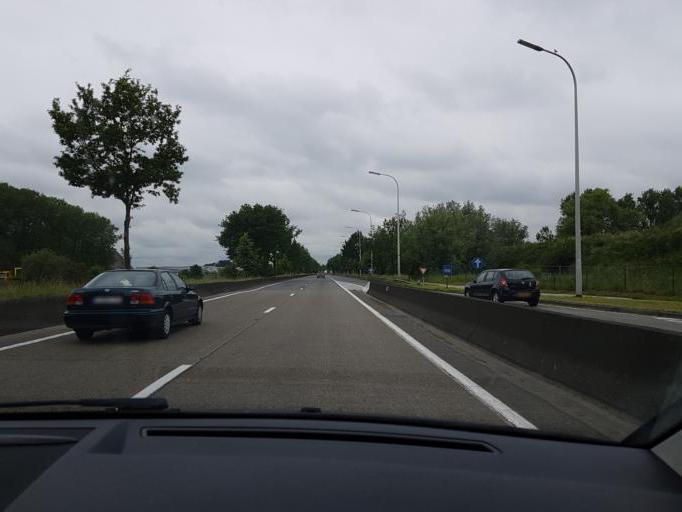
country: BE
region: Flanders
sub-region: Provincie Oost-Vlaanderen
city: Gent
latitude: 51.0535
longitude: 3.6728
